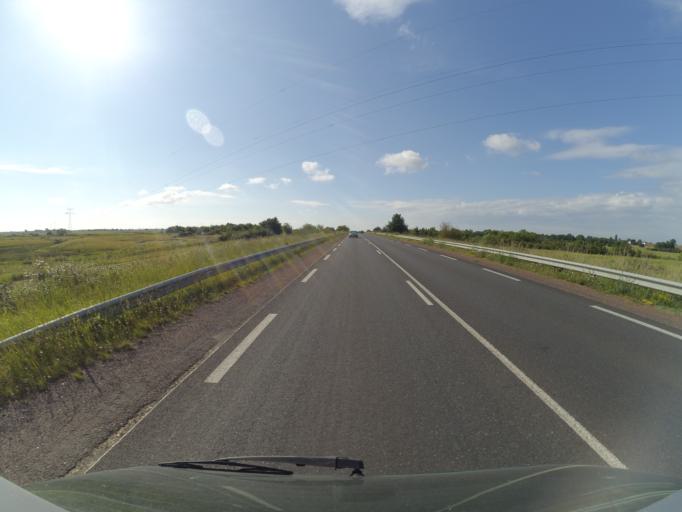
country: FR
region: Poitou-Charentes
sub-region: Departement de la Charente-Maritime
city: Saint-Agnant
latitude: 45.8540
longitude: -0.9614
